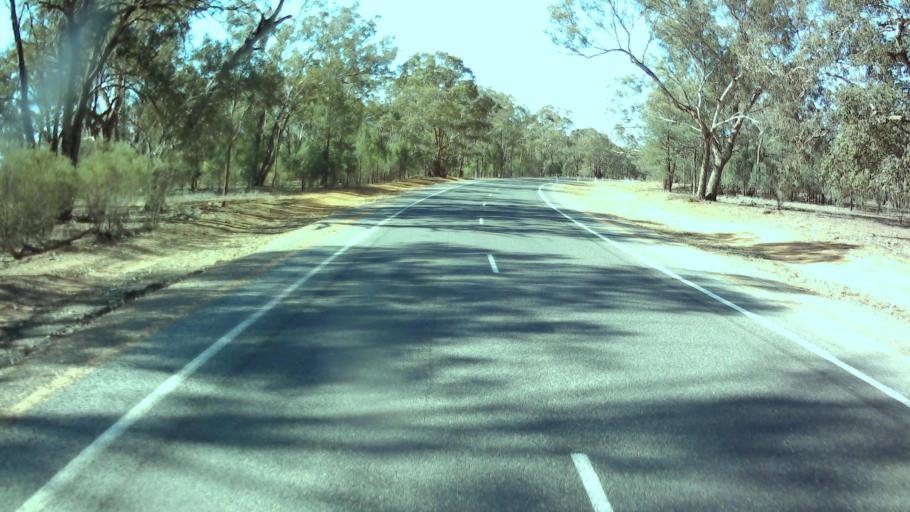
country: AU
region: New South Wales
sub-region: Weddin
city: Grenfell
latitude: -33.7560
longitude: 148.0826
